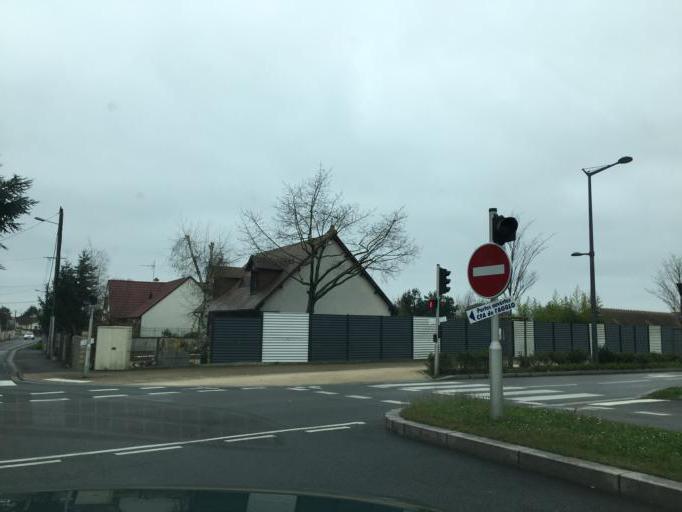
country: FR
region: Centre
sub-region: Departement du Loiret
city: Fleury-les-Aubrais
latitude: 47.9227
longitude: 1.9296
